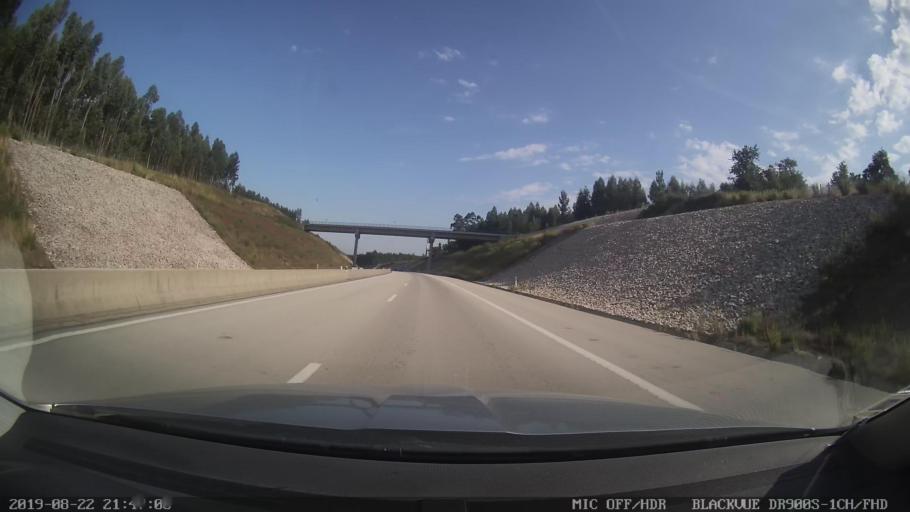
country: PT
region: Coimbra
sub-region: Penela
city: Penela
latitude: 39.9997
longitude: -8.3622
